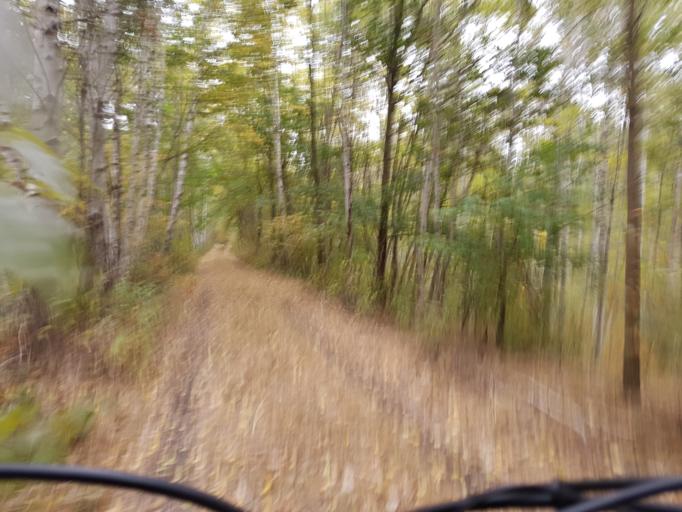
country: DE
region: Brandenburg
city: Trobitz
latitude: 51.5845
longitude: 13.4231
